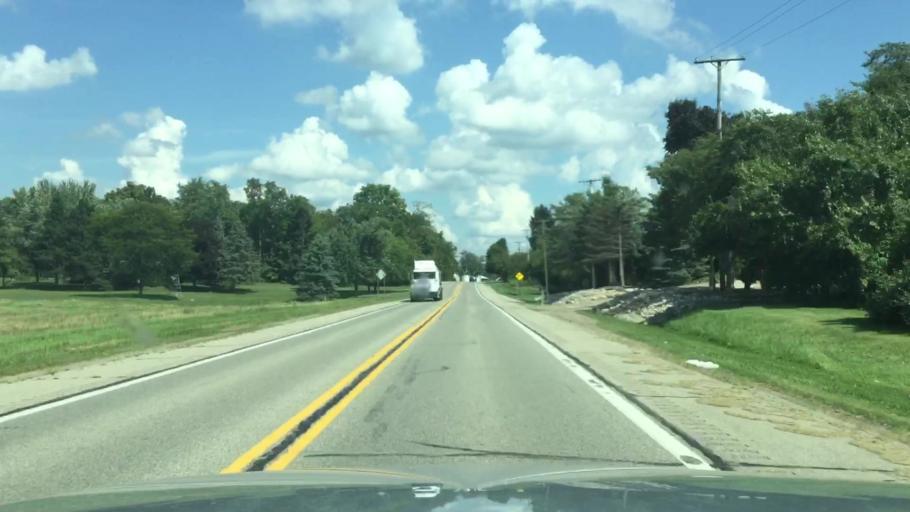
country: US
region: Michigan
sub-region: Lenawee County
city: Clinton
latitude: 42.0849
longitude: -83.9446
